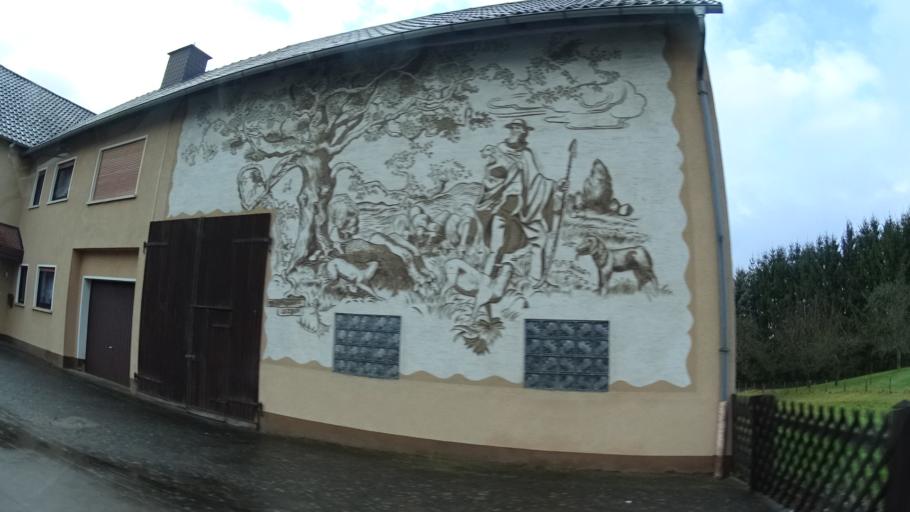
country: DE
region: Hesse
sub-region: Regierungsbezirk Kassel
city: Flieden
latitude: 50.4090
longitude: 9.5816
